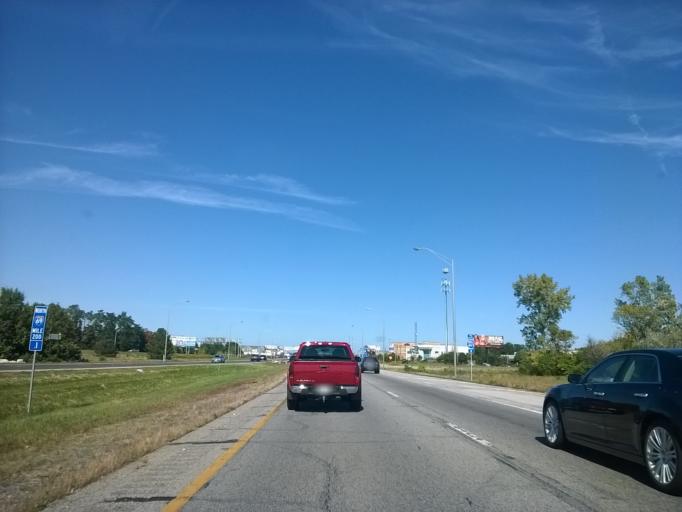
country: US
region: Indiana
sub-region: Marion County
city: Lawrence
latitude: 39.8957
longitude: -86.0533
